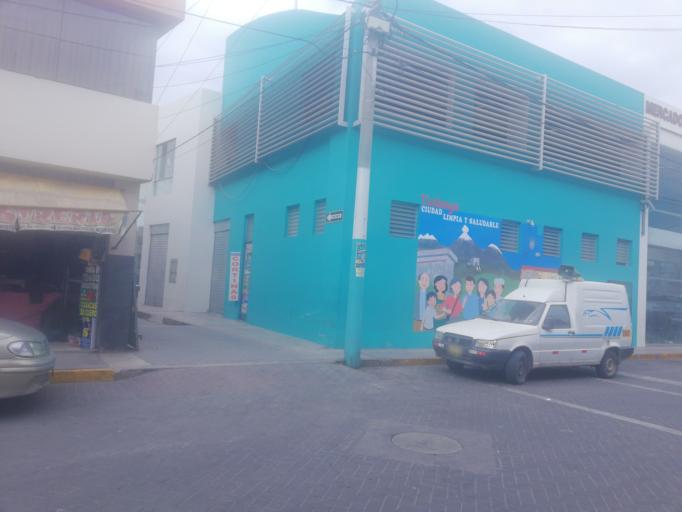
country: PE
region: Arequipa
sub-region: Provincia de Arequipa
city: Tiabaya
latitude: -16.4483
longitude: -71.5905
